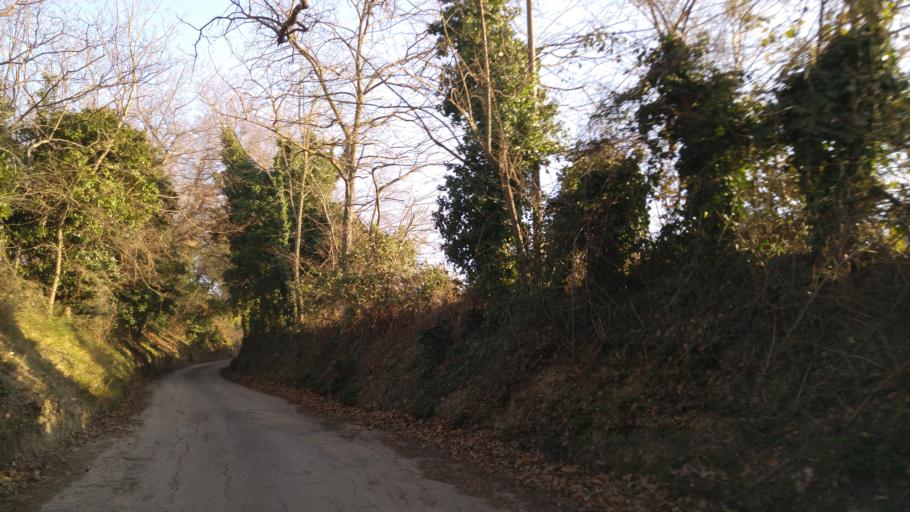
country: IT
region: The Marches
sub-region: Provincia di Pesaro e Urbino
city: Fenile
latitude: 43.8637
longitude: 12.9499
